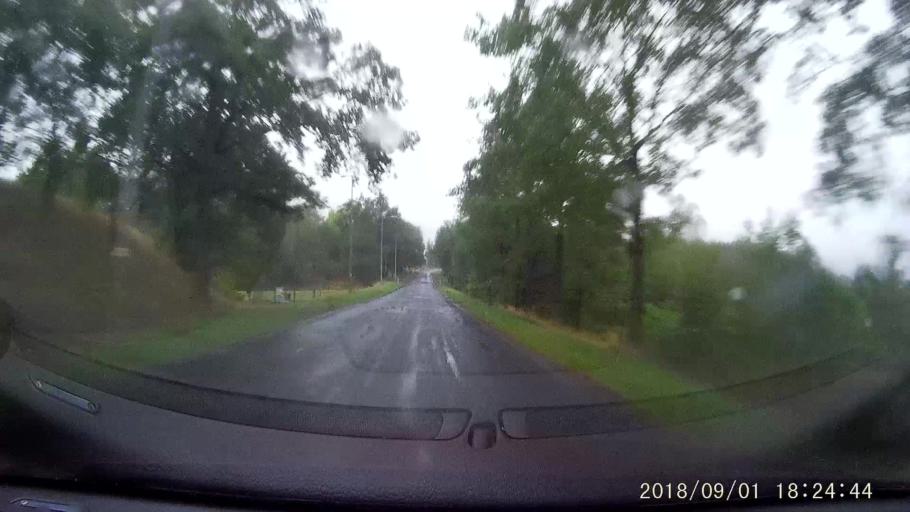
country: PL
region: Lower Silesian Voivodeship
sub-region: Powiat zgorzelecki
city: Piensk
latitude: 51.2345
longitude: 15.0342
